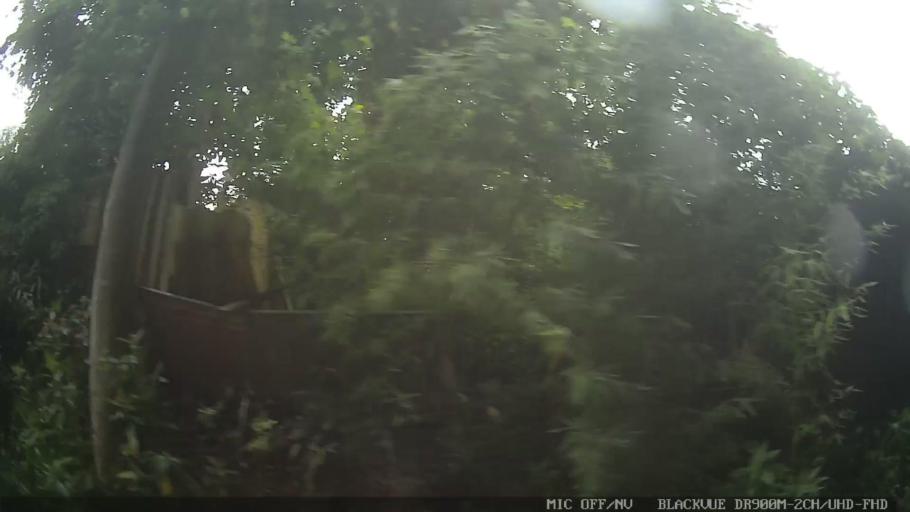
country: BR
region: Sao Paulo
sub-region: Suzano
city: Suzano
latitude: -23.6253
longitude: -46.2928
